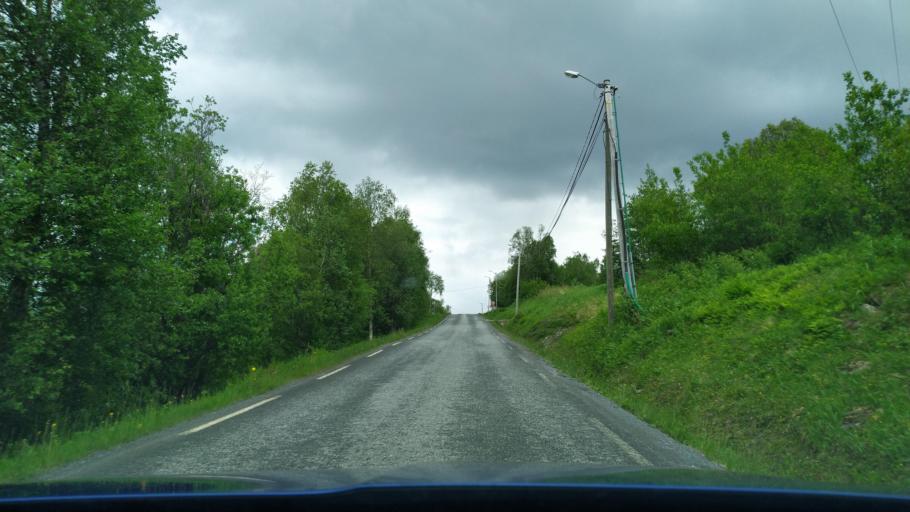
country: NO
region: Troms
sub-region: Tranoy
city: Vangsvika
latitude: 69.1265
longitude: 17.8566
